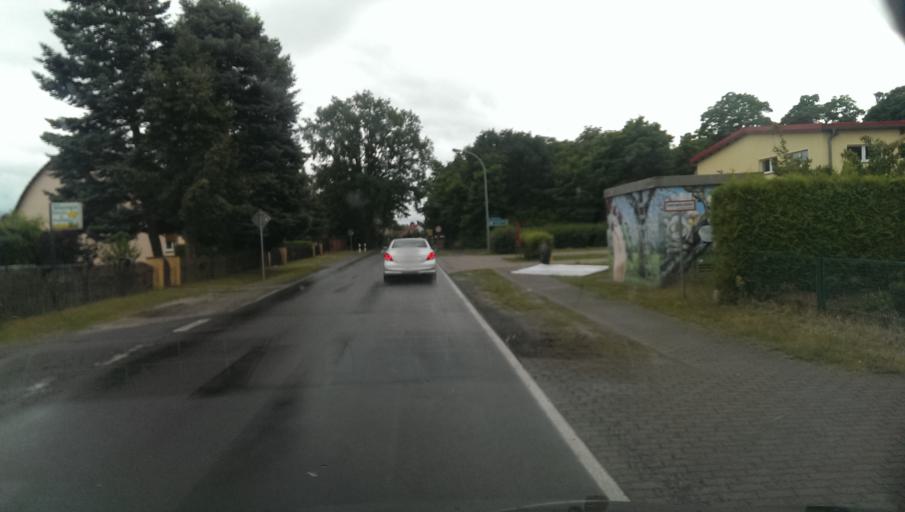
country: DE
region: Brandenburg
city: Gross Kreutz
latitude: 52.3925
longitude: 12.7110
